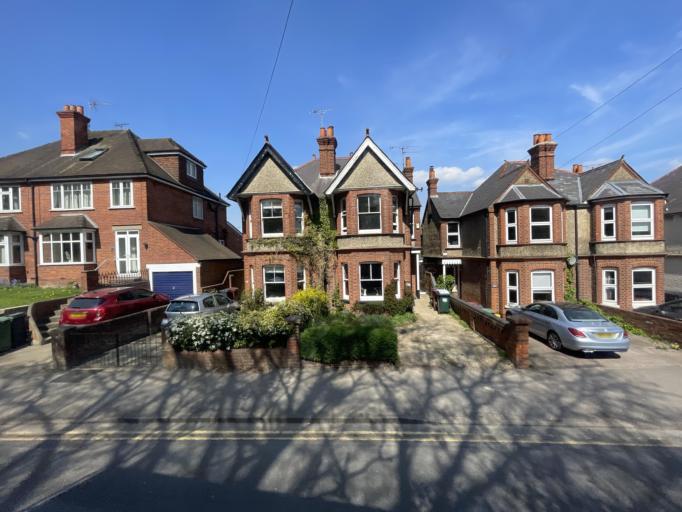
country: GB
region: England
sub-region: Reading
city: Reading
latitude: 51.4522
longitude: -1.0063
